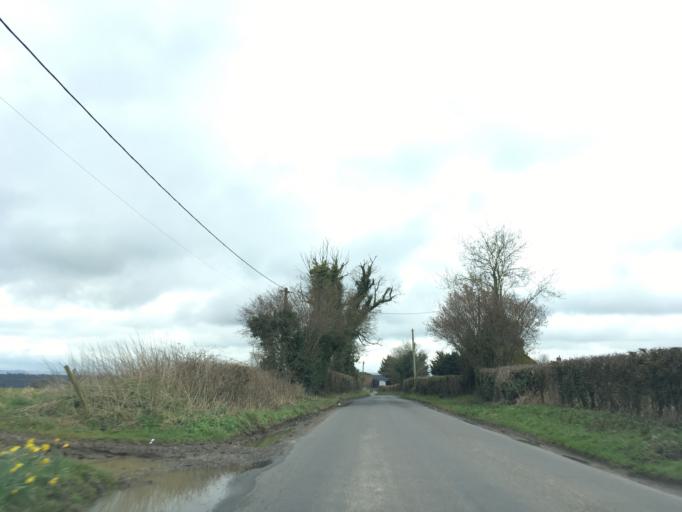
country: GB
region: England
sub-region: Wiltshire
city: Chilton Foliat
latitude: 51.4494
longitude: -1.5349
